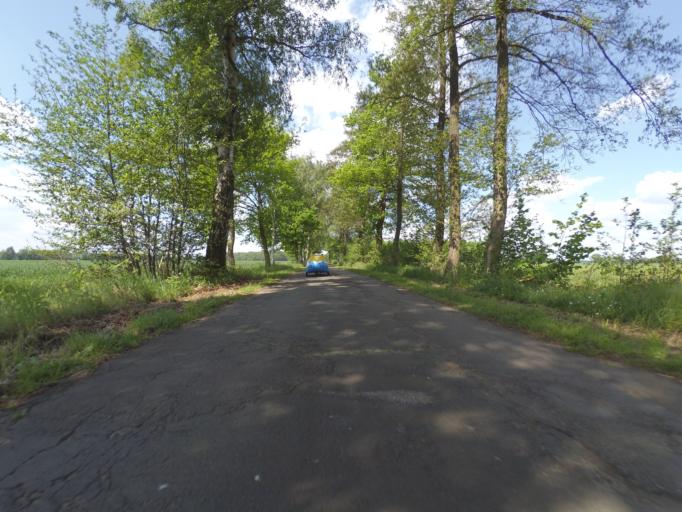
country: DE
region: Lower Saxony
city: Broeckel
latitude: 52.5053
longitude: 10.2509
